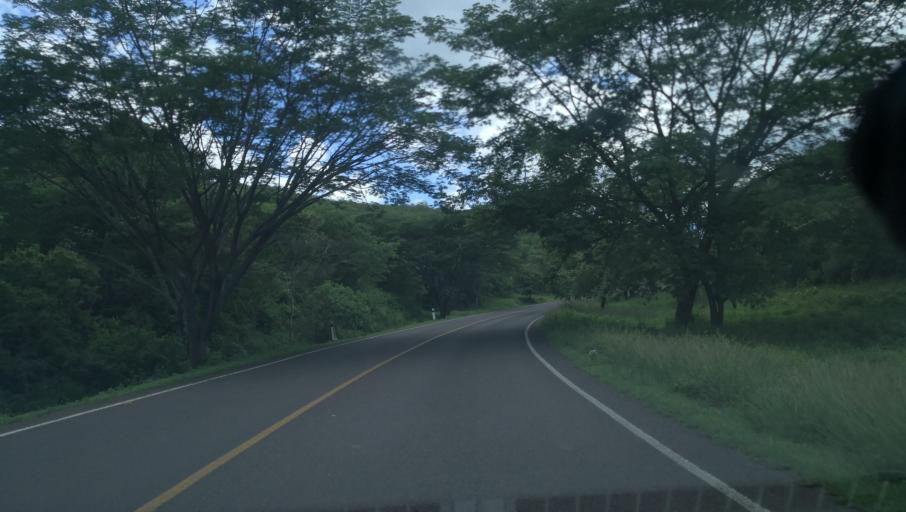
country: NI
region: Madriz
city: Palacaguina
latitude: 13.4334
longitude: -86.4255
